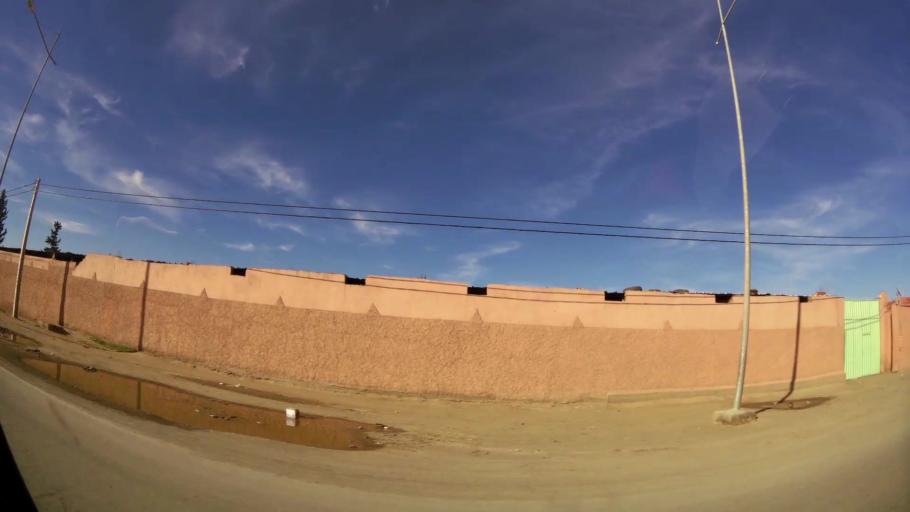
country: MA
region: Marrakech-Tensift-Al Haouz
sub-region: Marrakech
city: Marrakesh
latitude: 31.7177
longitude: -8.0799
